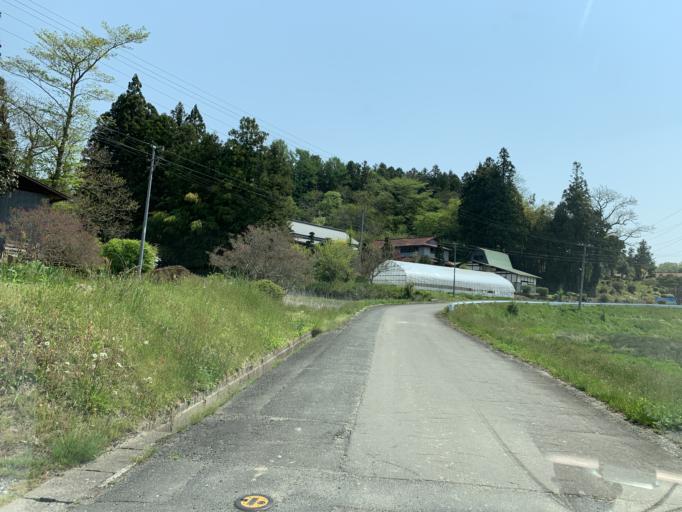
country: JP
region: Iwate
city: Ichinoseki
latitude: 38.8568
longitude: 141.0838
